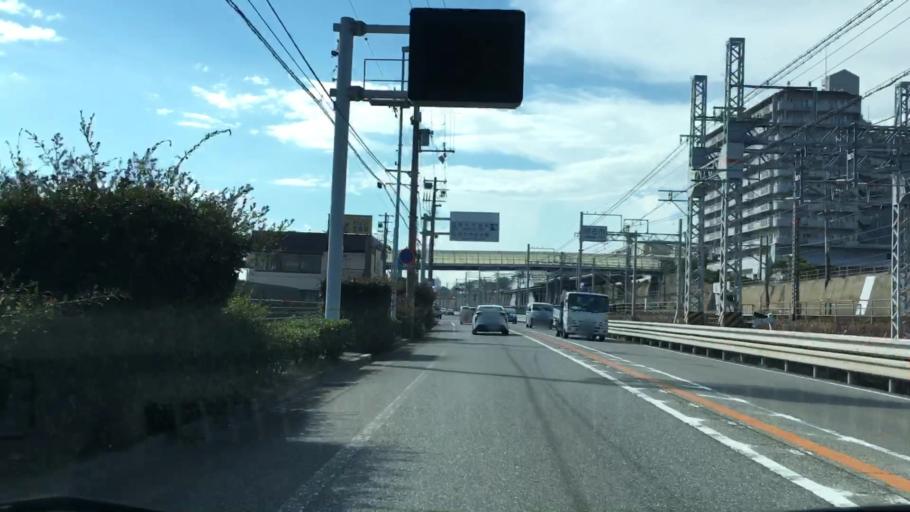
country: JP
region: Hyogo
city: Akashi
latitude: 34.6432
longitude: 135.0193
